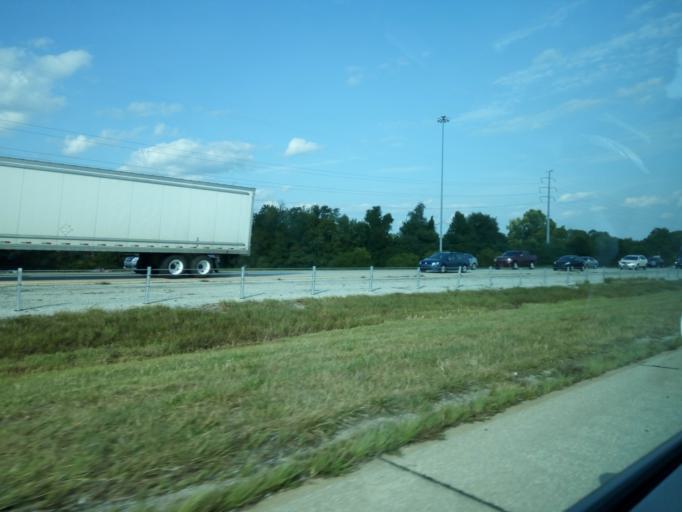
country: US
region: Kentucky
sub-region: Jefferson County
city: Worthington Hills
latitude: 38.2860
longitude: -85.5115
